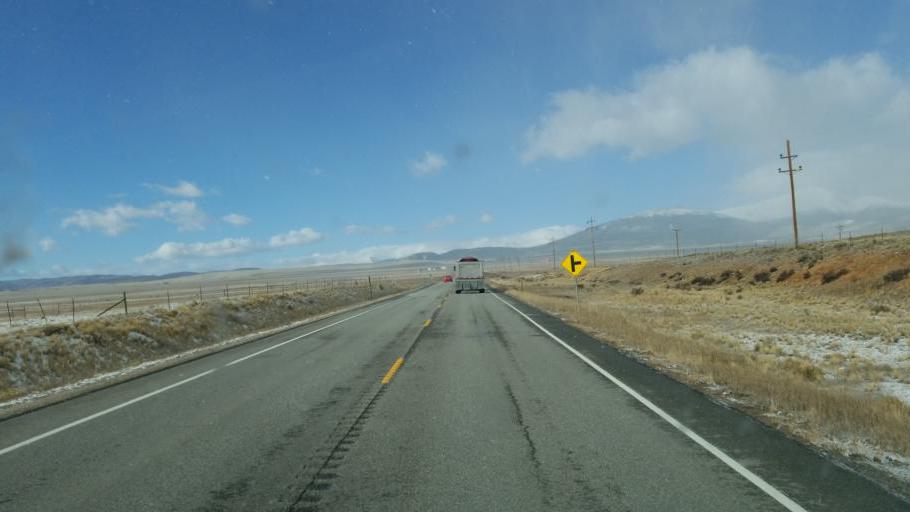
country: US
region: Colorado
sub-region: Park County
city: Fairplay
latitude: 39.3561
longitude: -105.8209
